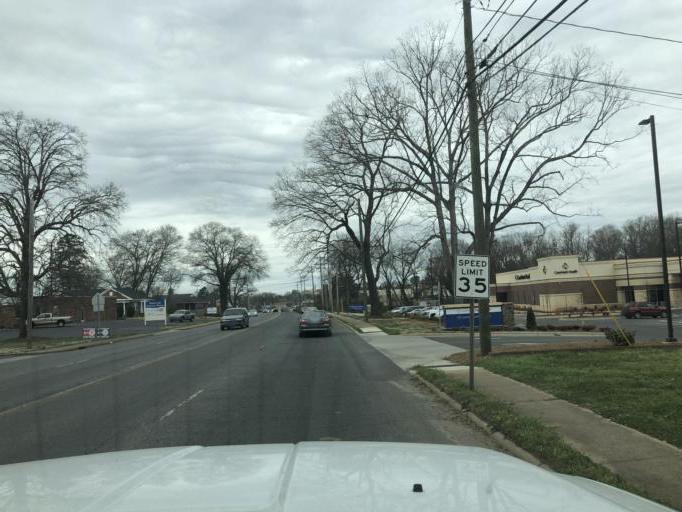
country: US
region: North Carolina
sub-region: Gaston County
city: Dallas
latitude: 35.3168
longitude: -81.1821
